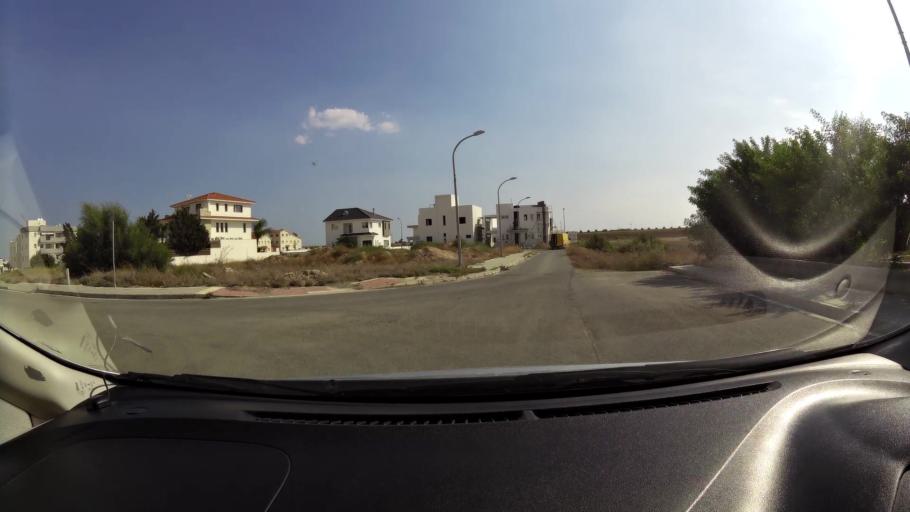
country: CY
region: Larnaka
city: Dhromolaxia
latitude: 34.9037
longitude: 33.5823
